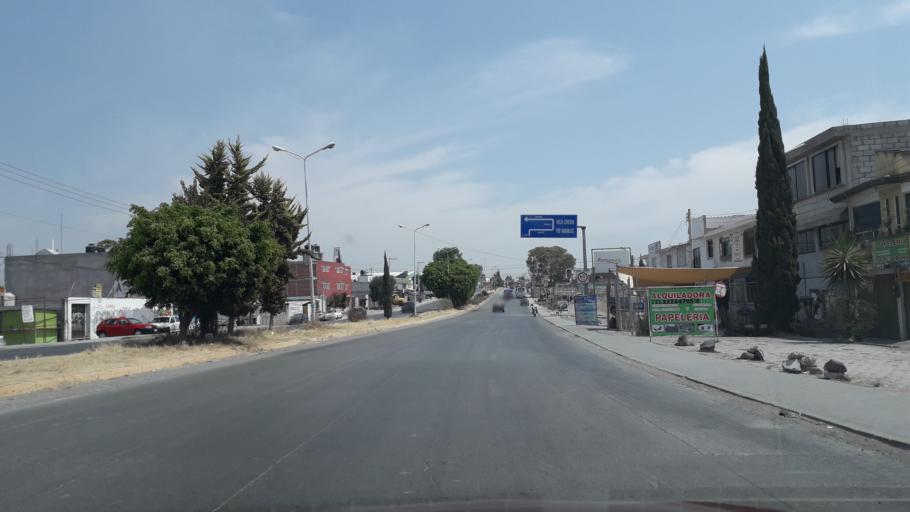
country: MX
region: Puebla
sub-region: Puebla
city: El Capulo (La Quebradora)
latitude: 18.9653
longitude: -98.2676
